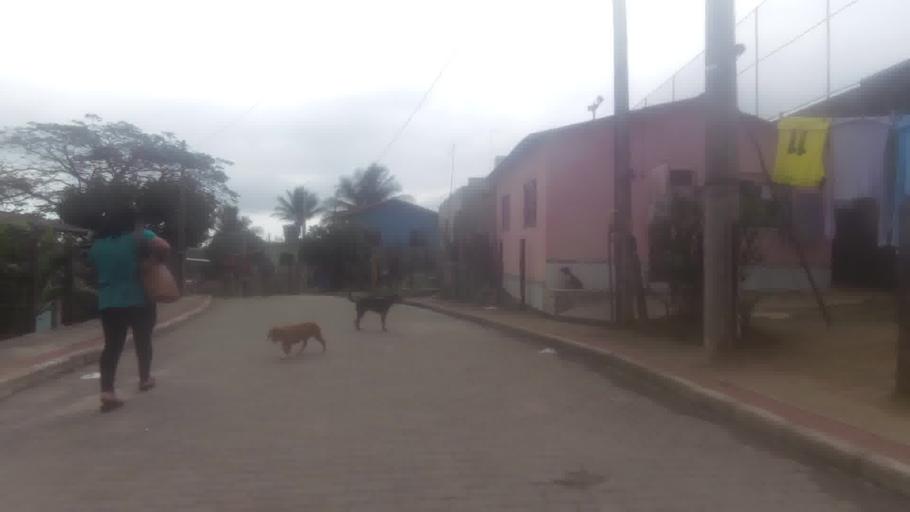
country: BR
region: Espirito Santo
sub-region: Piuma
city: Piuma
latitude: -20.7954
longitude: -40.6034
